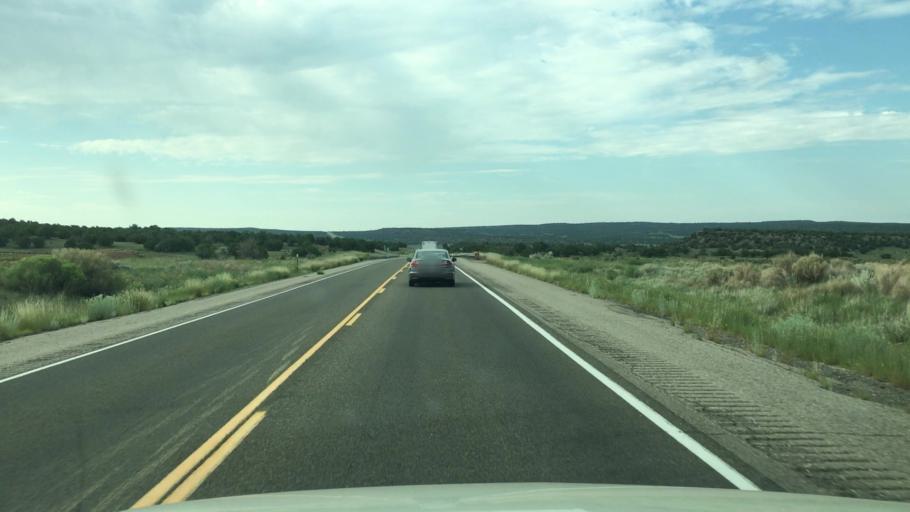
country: US
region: New Mexico
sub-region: Santa Fe County
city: Eldorado at Santa Fe
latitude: 35.2665
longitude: -105.8090
